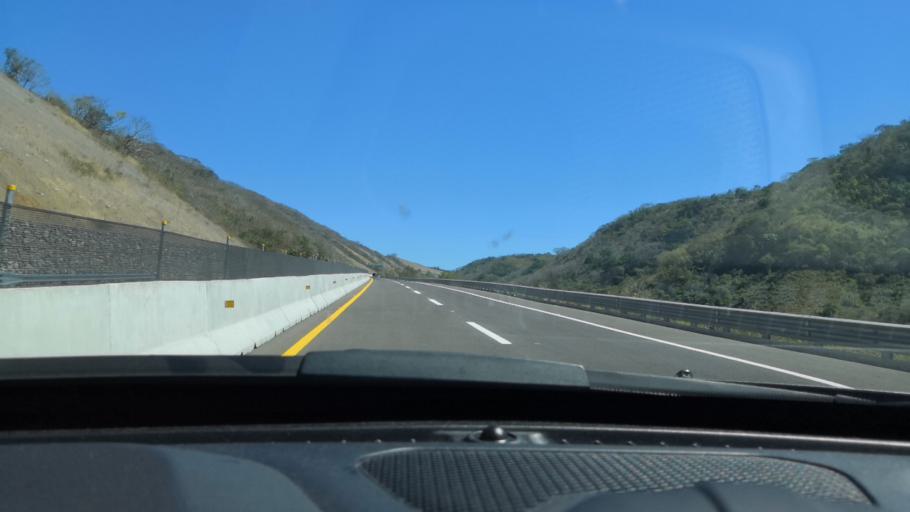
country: MX
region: Nayarit
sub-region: Compostela
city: Juan Escutia (Borbollon)
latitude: 21.1314
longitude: -104.9045
